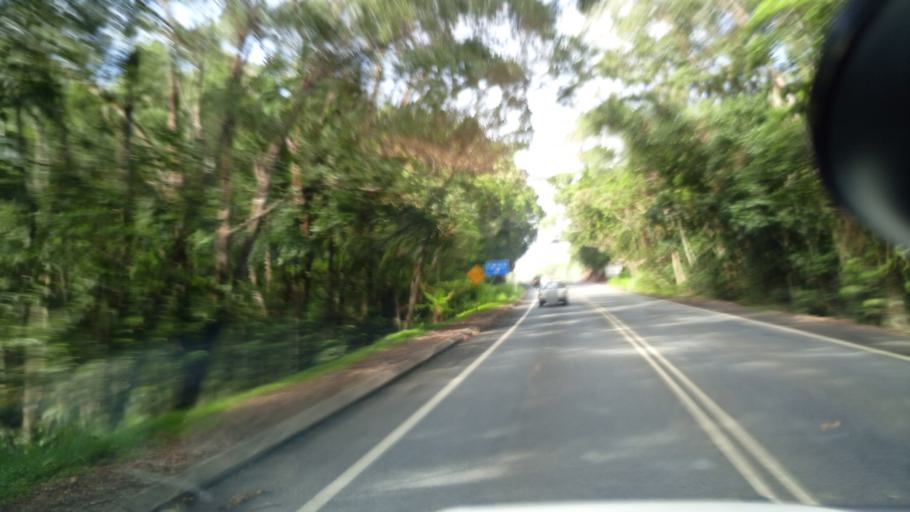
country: AU
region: Queensland
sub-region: Tablelands
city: Kuranda
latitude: -16.8218
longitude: 145.6273
